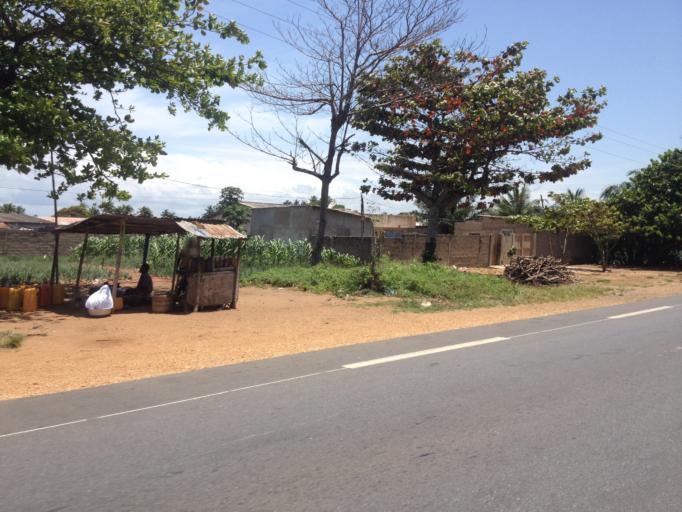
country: BJ
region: Mono
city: Grand-Popo
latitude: 6.2682
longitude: 1.7749
